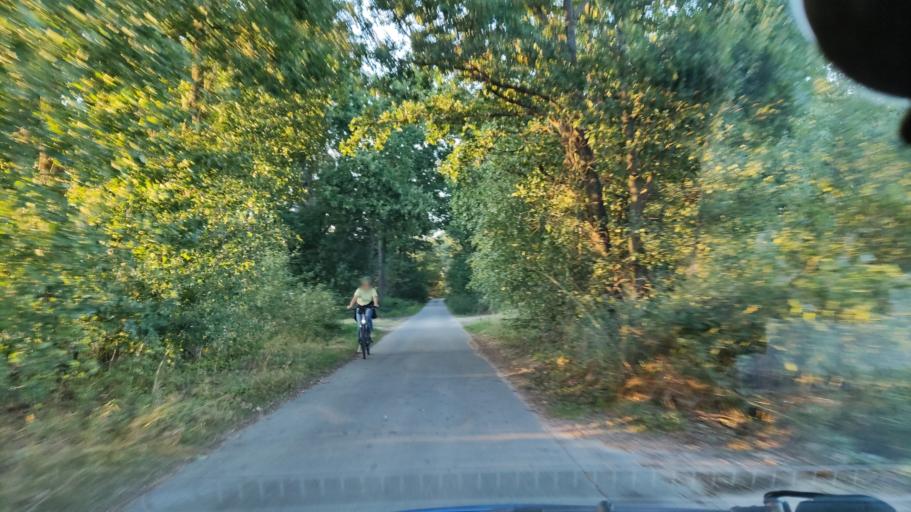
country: DE
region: Lower Saxony
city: Eimke
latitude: 52.9690
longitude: 10.3573
